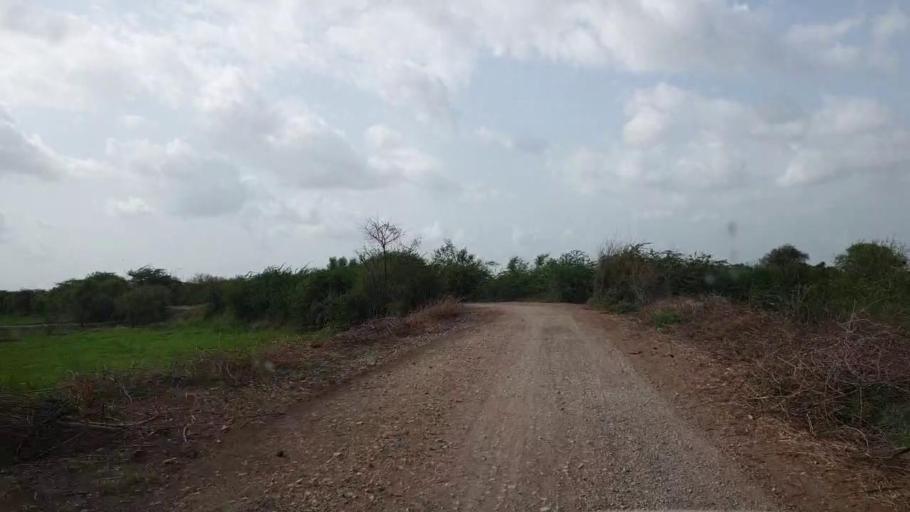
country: PK
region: Sindh
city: Kario
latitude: 24.6965
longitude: 68.6485
